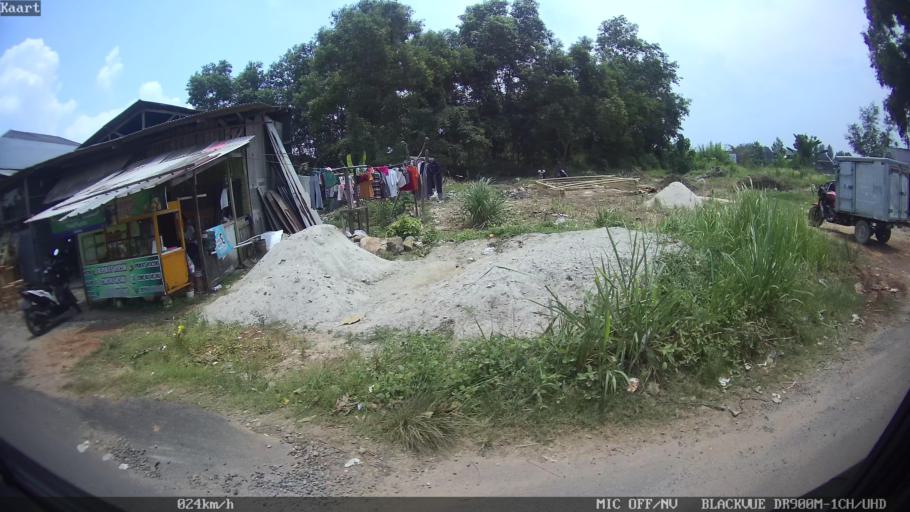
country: ID
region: Lampung
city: Kedaton
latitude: -5.3525
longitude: 105.2396
